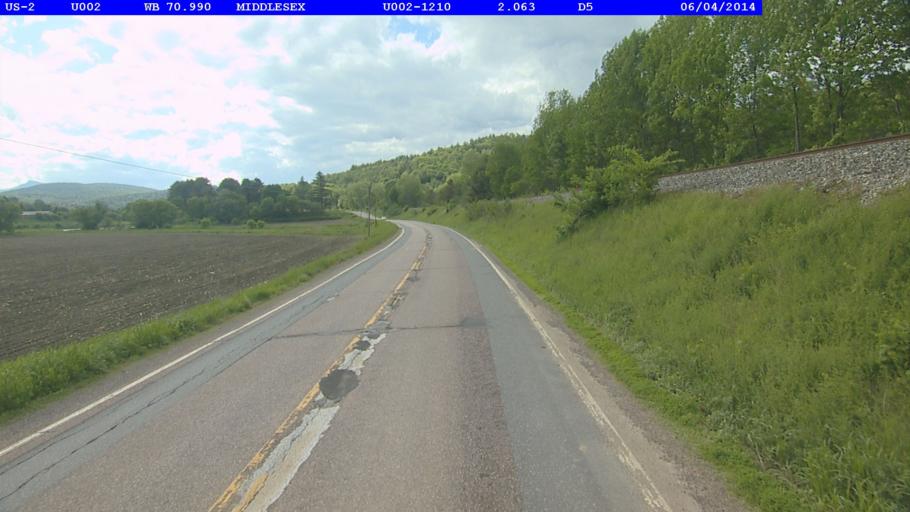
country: US
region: Vermont
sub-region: Washington County
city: Montpelier
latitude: 44.2888
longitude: -72.6659
